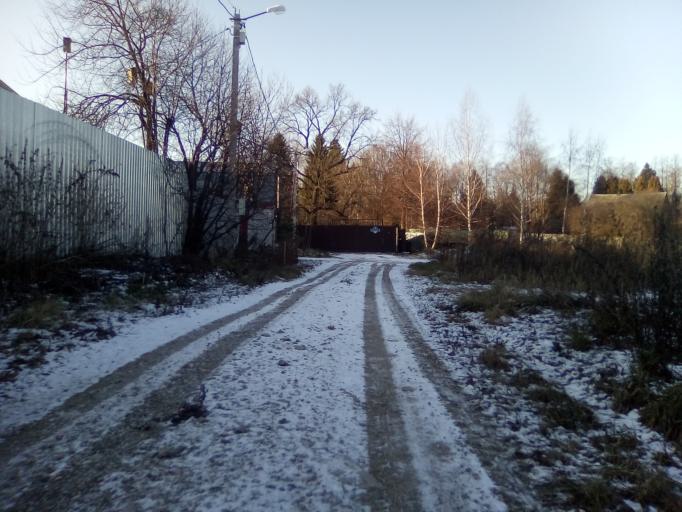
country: RU
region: Moskovskaya
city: Lesnoy Gorodok
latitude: 55.6492
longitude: 37.1700
